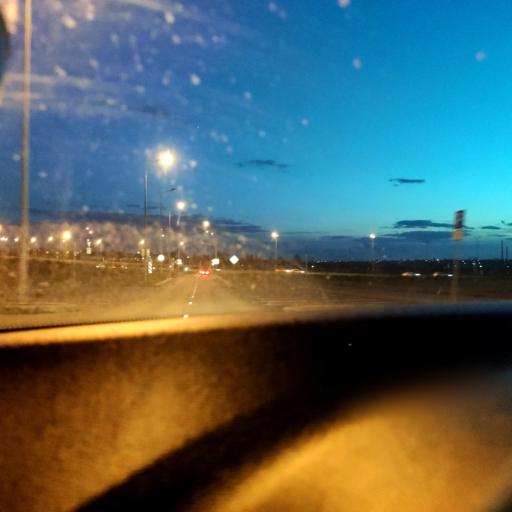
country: RU
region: Samara
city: Petra-Dubrava
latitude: 53.2964
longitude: 50.3289
